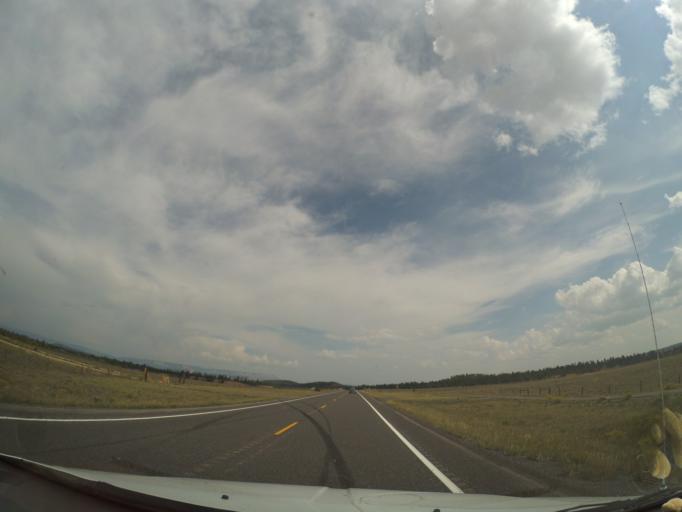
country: US
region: Utah
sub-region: Garfield County
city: Panguitch
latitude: 37.7144
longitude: -112.2264
